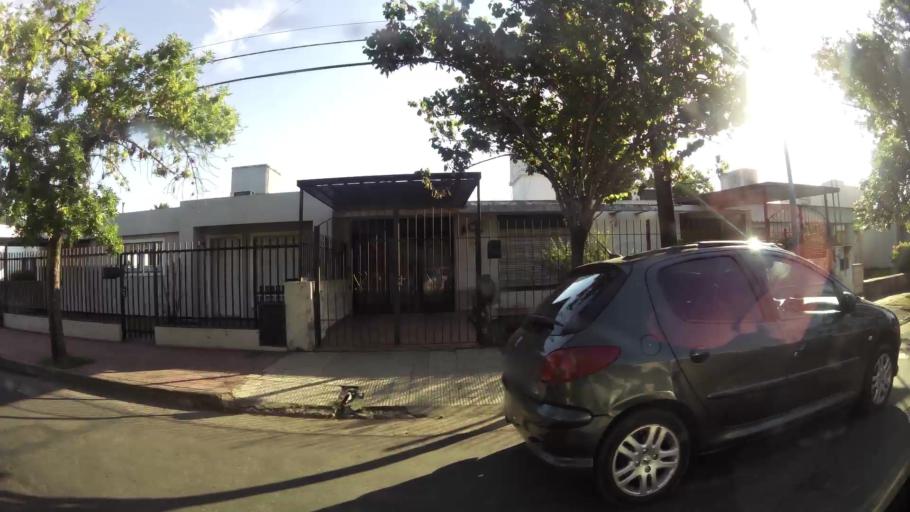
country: AR
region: Cordoba
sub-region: Departamento de Capital
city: Cordoba
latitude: -31.3818
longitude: -64.2332
